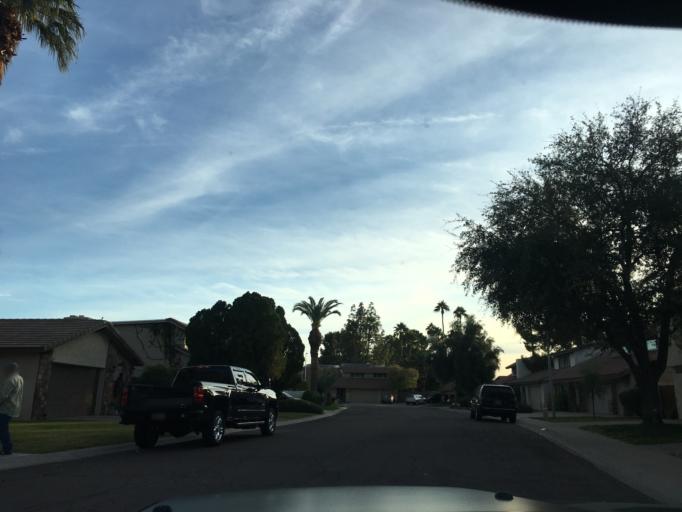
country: US
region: Arizona
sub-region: Maricopa County
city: Tempe
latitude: 33.3768
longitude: -111.9140
